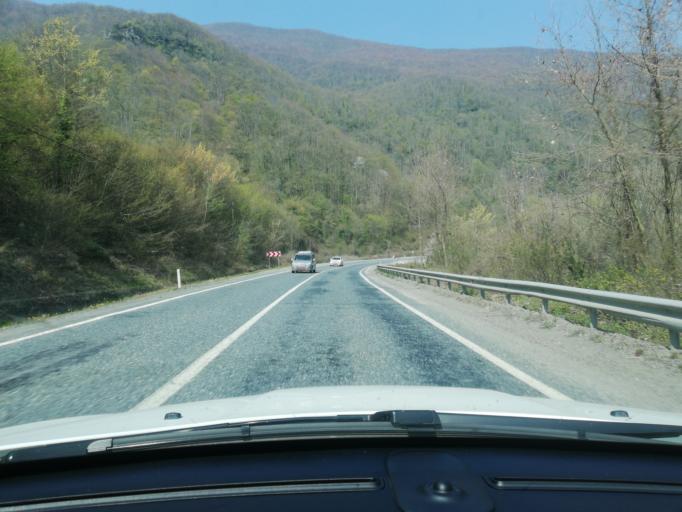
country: TR
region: Zonguldak
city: Gokcebey
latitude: 41.2640
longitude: 32.1575
